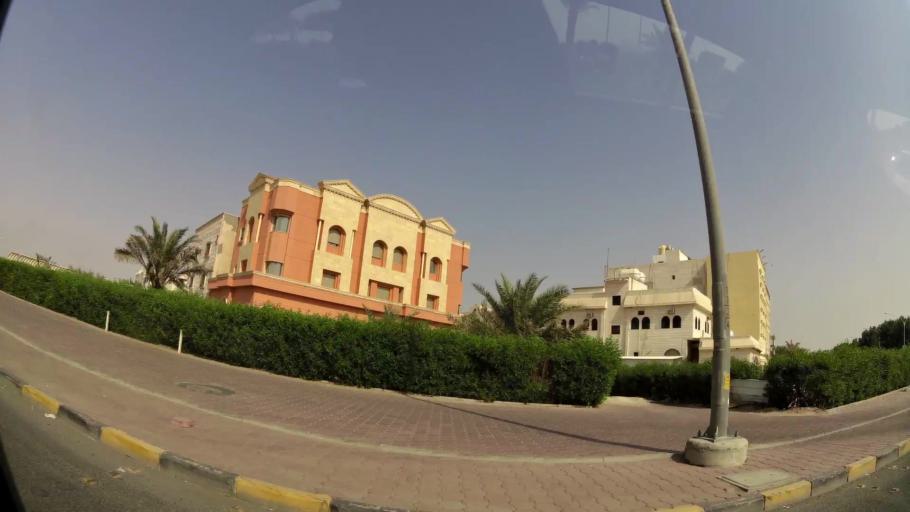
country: KW
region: Muhafazat al Jahra'
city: Al Jahra'
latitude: 29.3320
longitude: 47.6484
